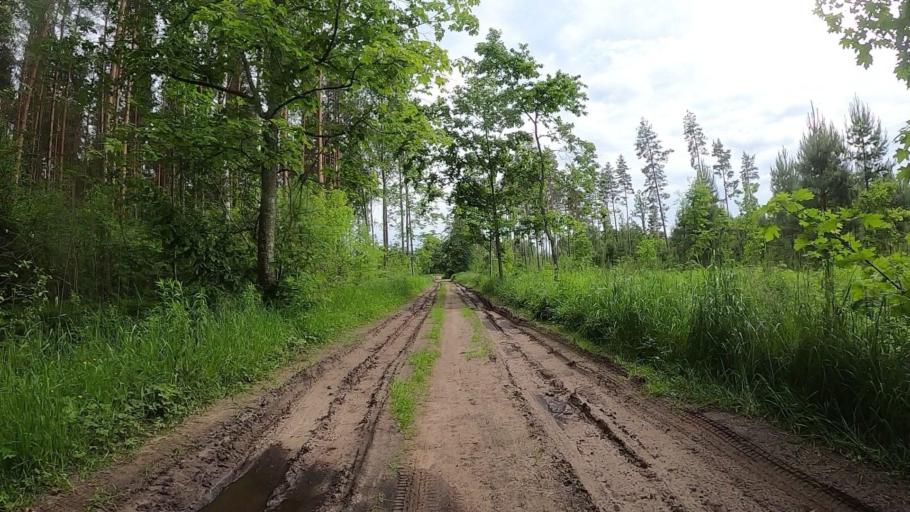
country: LV
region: Olaine
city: Olaine
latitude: 56.7433
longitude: 23.8705
